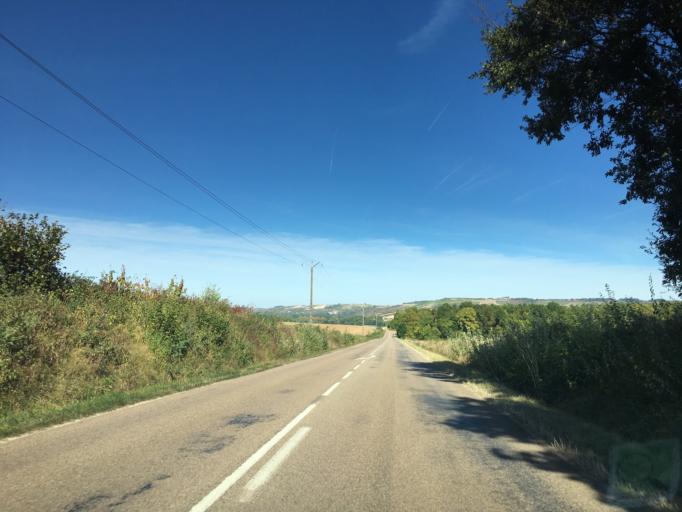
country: FR
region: Bourgogne
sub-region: Departement de l'Yonne
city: Saint-Bris-le-Vineux
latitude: 47.6796
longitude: 3.6556
